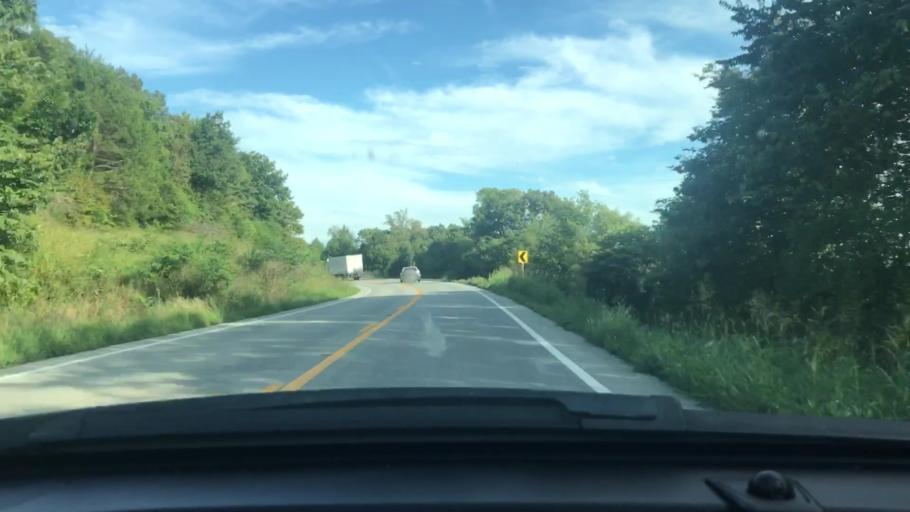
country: US
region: Arkansas
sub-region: Sharp County
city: Cherokee Village
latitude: 36.2979
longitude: -91.4375
